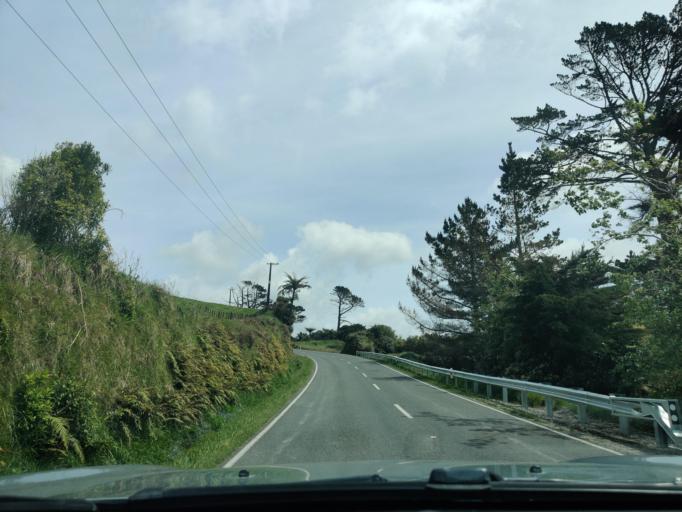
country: NZ
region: Taranaki
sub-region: South Taranaki District
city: Eltham
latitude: -39.3753
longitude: 174.1836
